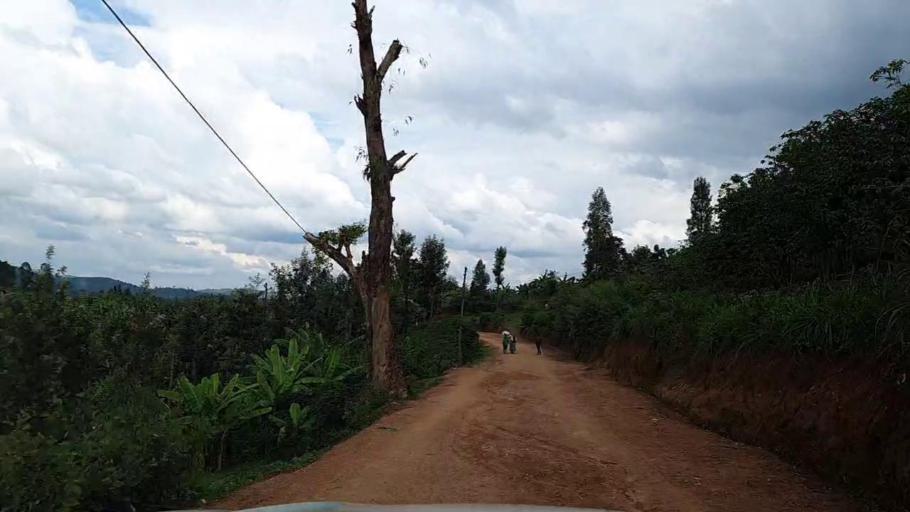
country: RW
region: Southern Province
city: Gikongoro
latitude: -2.4224
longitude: 29.6479
